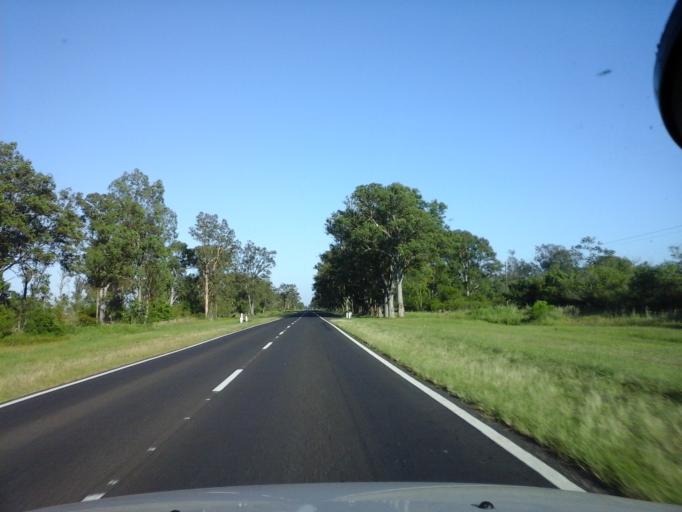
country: AR
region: Corrientes
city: Ita Ibate
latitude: -27.4572
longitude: -57.3207
